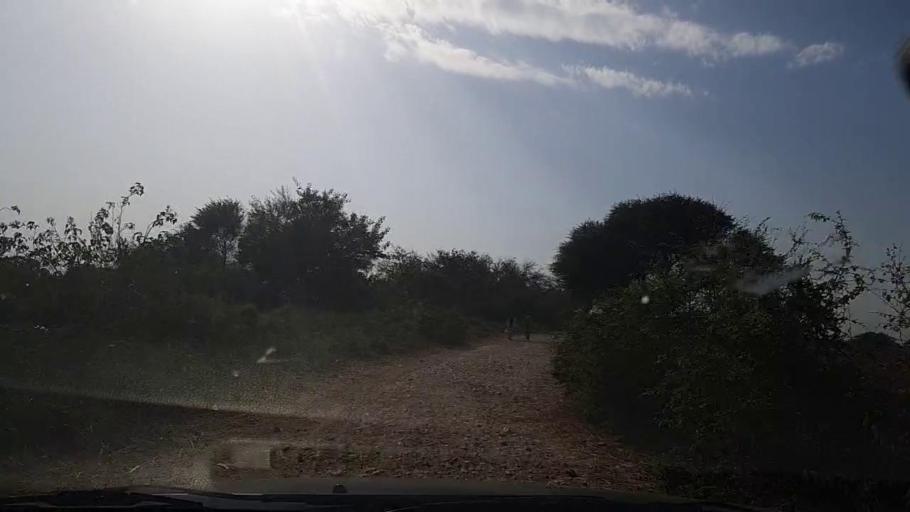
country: PK
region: Sindh
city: Mirpur Batoro
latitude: 24.5528
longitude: 68.1746
